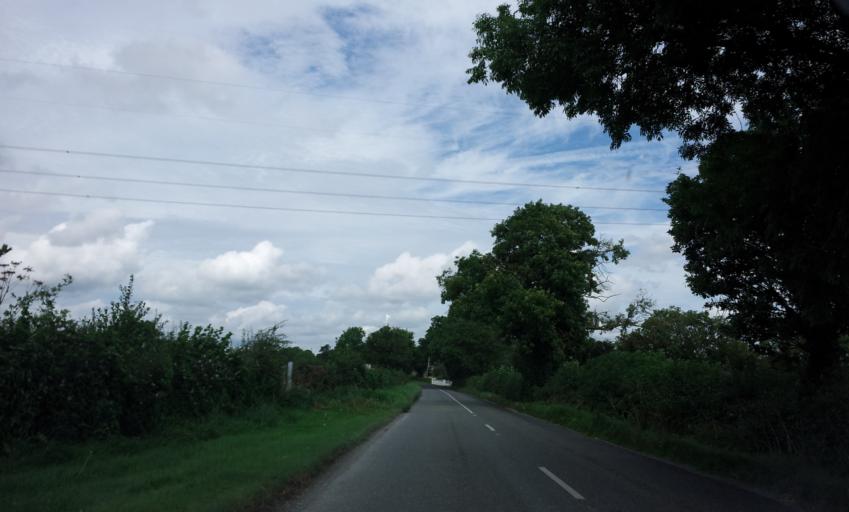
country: IE
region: Leinster
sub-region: Laois
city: Stradbally
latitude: 52.9922
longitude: -7.2207
